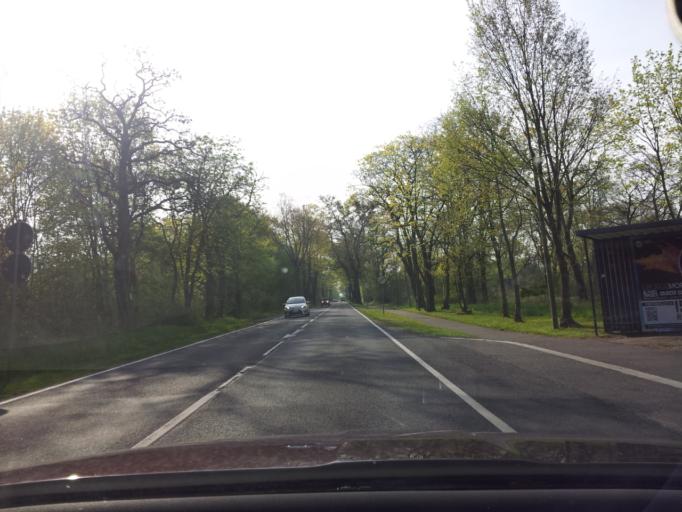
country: DE
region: Brandenburg
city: Niedergorsdorf
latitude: 52.0038
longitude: 13.0217
